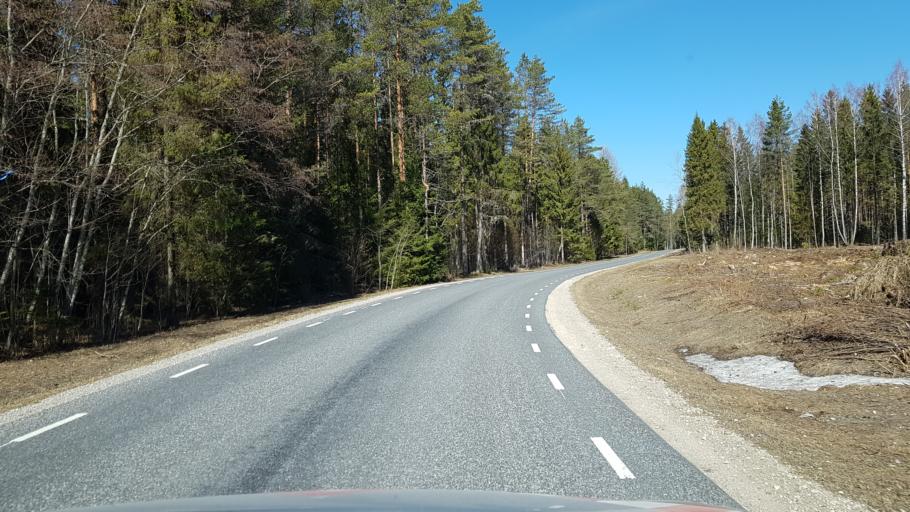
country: EE
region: Laeaene-Virumaa
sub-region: Vinni vald
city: Vinni
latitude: 59.1267
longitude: 26.5209
